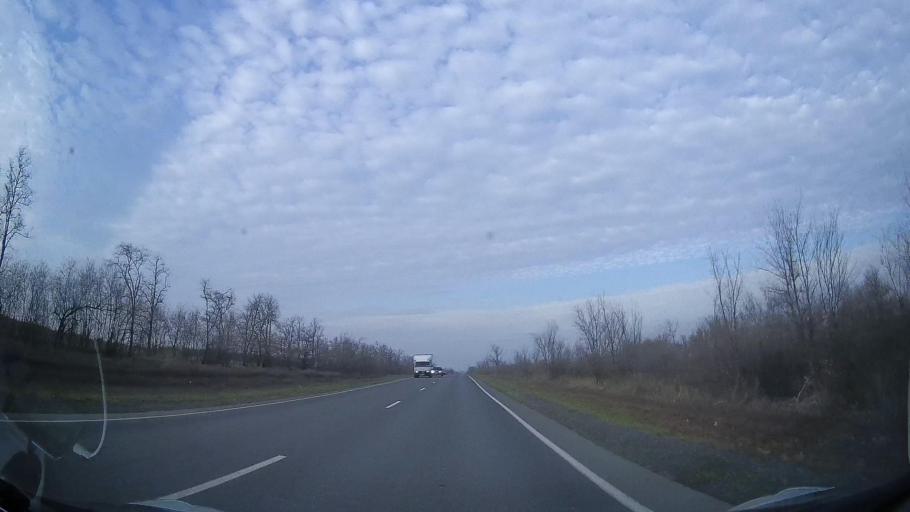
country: RU
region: Rostov
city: Bagayevskaya
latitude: 47.1534
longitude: 40.2765
